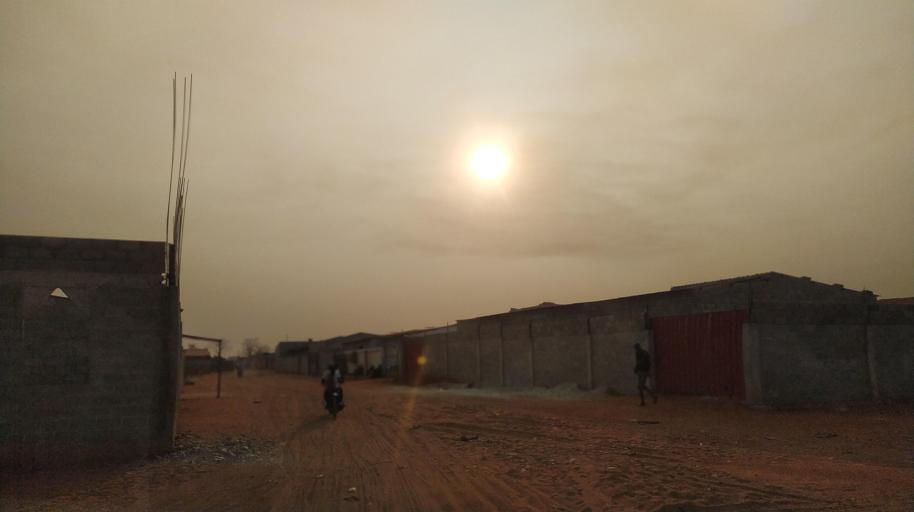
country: AO
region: Luanda
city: Luanda
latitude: -9.0730
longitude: 13.4214
